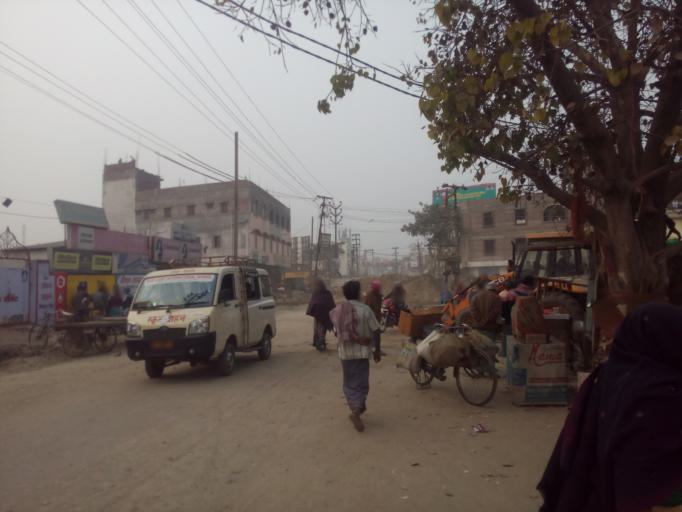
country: IN
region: Bihar
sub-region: Muzaffarpur
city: Muzaffarpur
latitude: 26.1030
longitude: 85.3999
